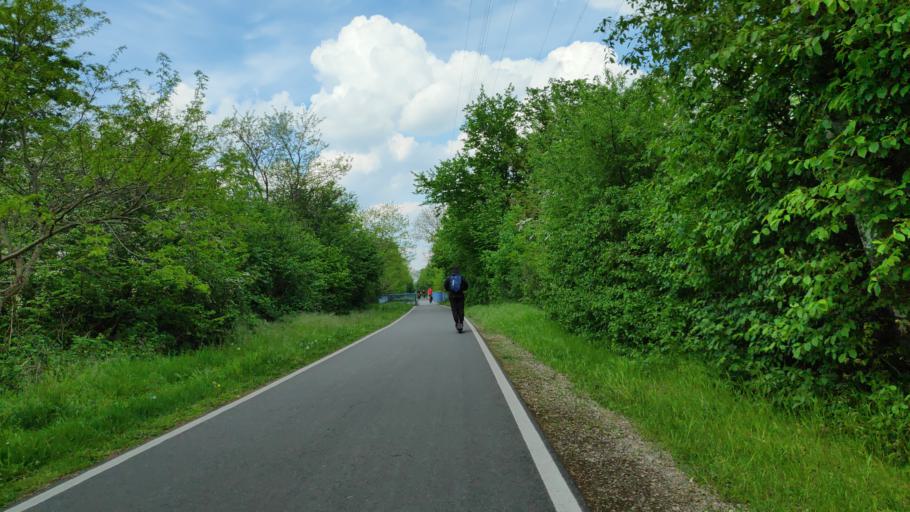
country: DE
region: North Rhine-Westphalia
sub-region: Regierungsbezirk Munster
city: Gelsenkirchen
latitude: 51.5259
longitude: 7.1375
